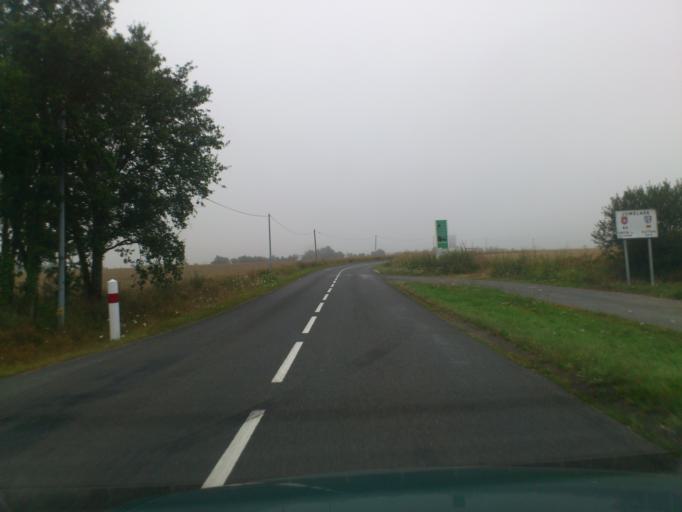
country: FR
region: Pays de la Loire
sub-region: Departement de la Loire-Atlantique
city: Saint-Hilaire-de-Clisson
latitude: 47.0399
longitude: -1.3249
